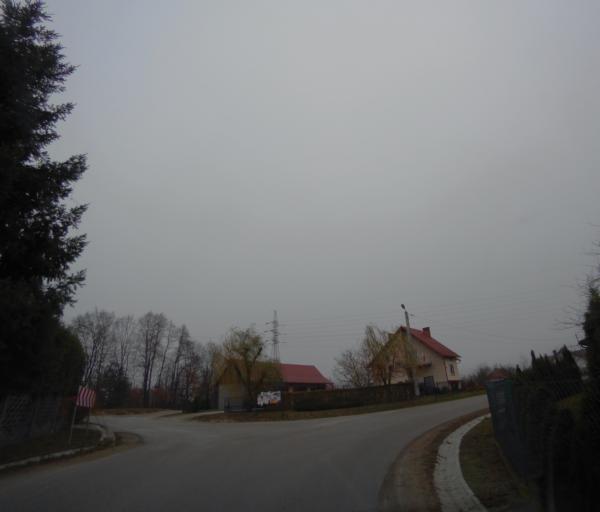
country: PL
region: Subcarpathian Voivodeship
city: Nowa Sarzyna
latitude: 50.2885
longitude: 22.3541
